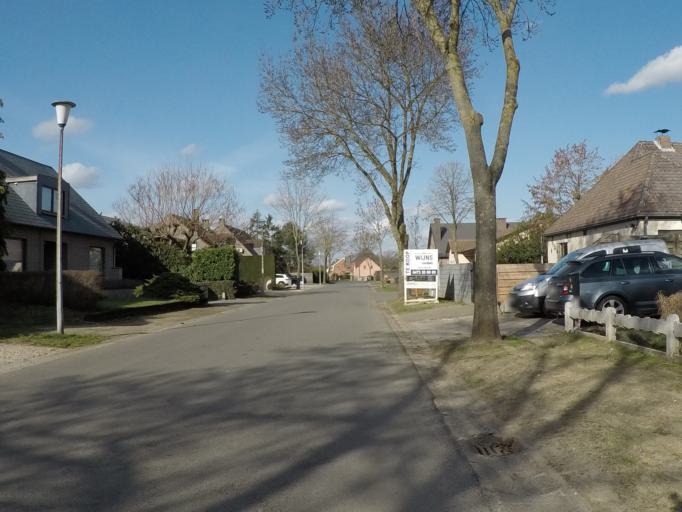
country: BE
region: Flanders
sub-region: Provincie Antwerpen
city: Nijlen
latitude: 51.1673
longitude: 4.6822
